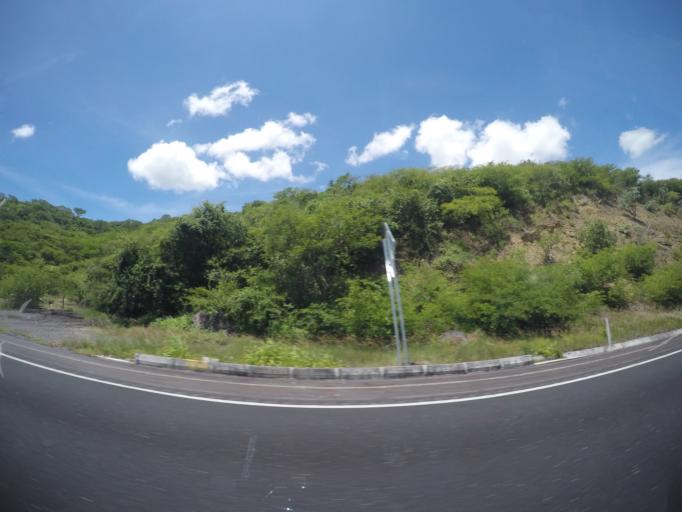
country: MX
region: Morelos
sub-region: Jojutla
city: Higueron
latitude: 18.4943
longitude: -99.1840
